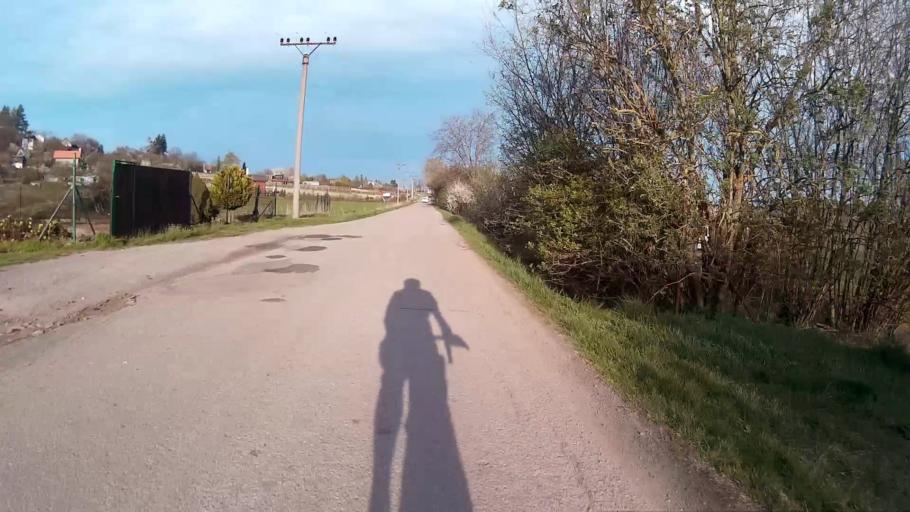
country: CZ
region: South Moravian
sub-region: Mesto Brno
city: Mokra Hora
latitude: 49.2421
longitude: 16.5573
